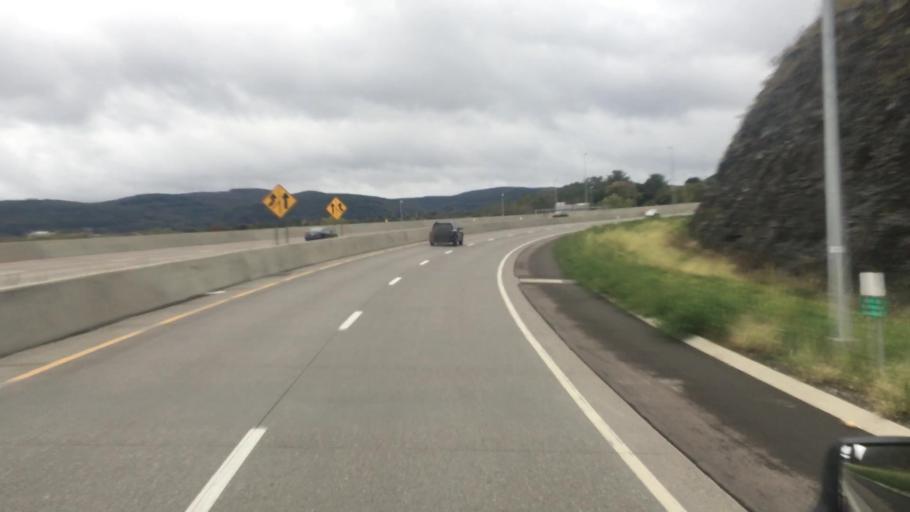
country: US
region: New York
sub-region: Broome County
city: Binghamton
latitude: 42.1128
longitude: -75.9114
